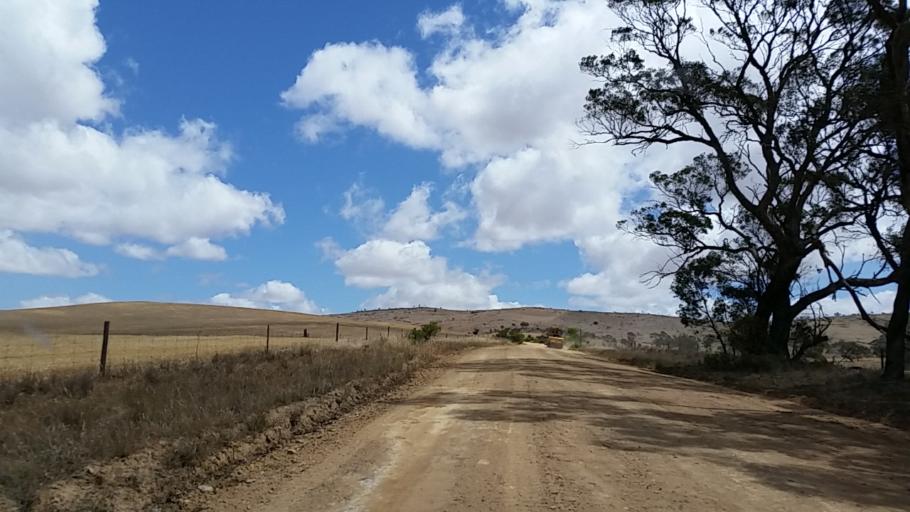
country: AU
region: South Australia
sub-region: Northern Areas
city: Jamestown
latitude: -32.9604
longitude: 138.5053
